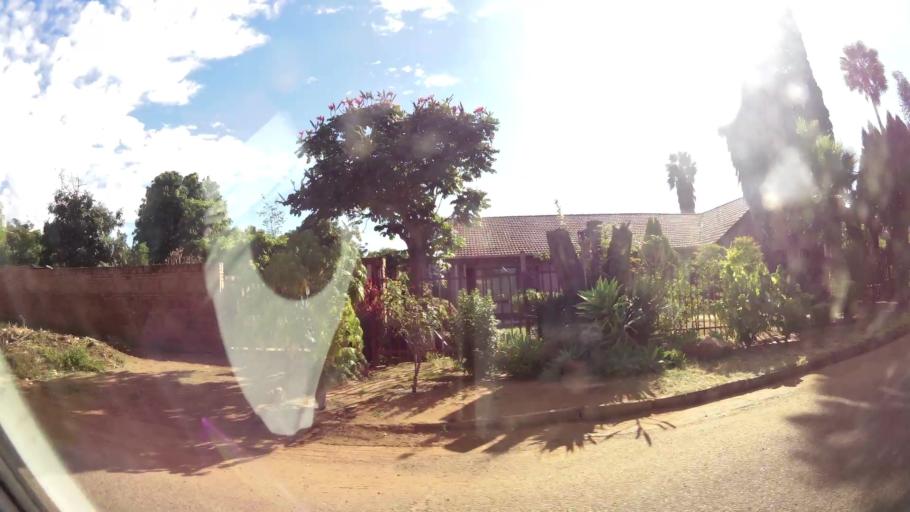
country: ZA
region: Limpopo
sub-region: Waterberg District Municipality
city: Warmbaths
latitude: -24.8804
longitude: 28.2756
